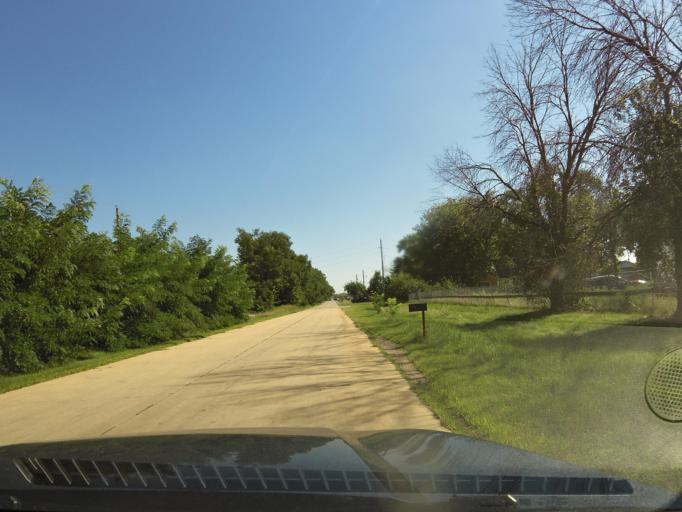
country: US
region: Iowa
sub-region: Black Hawk County
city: Waterloo
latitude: 42.4729
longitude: -92.3190
